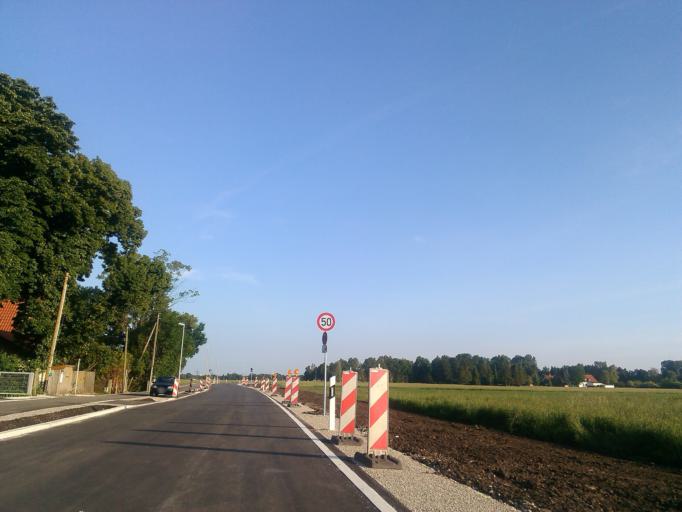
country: DE
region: Bavaria
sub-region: Upper Bavaria
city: Grobenzell
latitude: 48.1932
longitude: 11.4074
